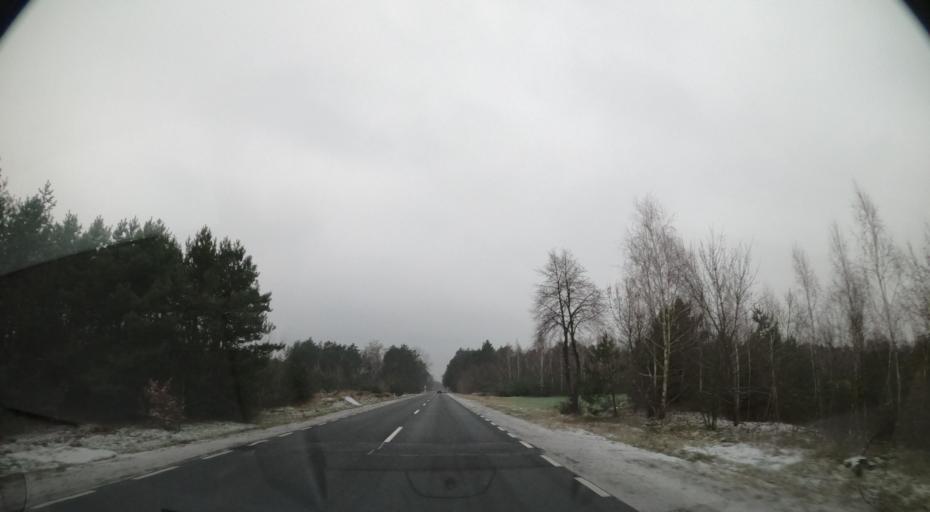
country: PL
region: Masovian Voivodeship
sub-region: Powiat plocki
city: Mala Wies
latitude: 52.4161
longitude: 20.1034
